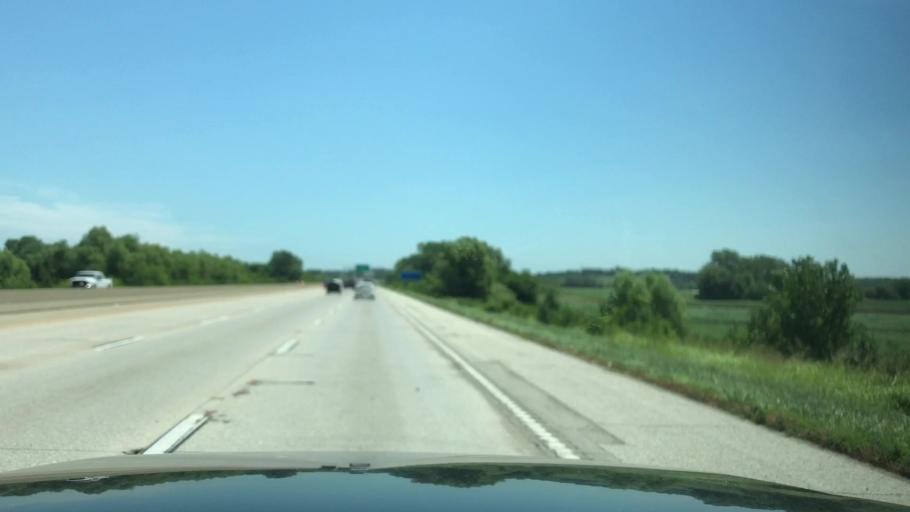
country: US
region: Missouri
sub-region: Saint Louis County
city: Bridgeton
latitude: 38.7910
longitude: -90.4384
